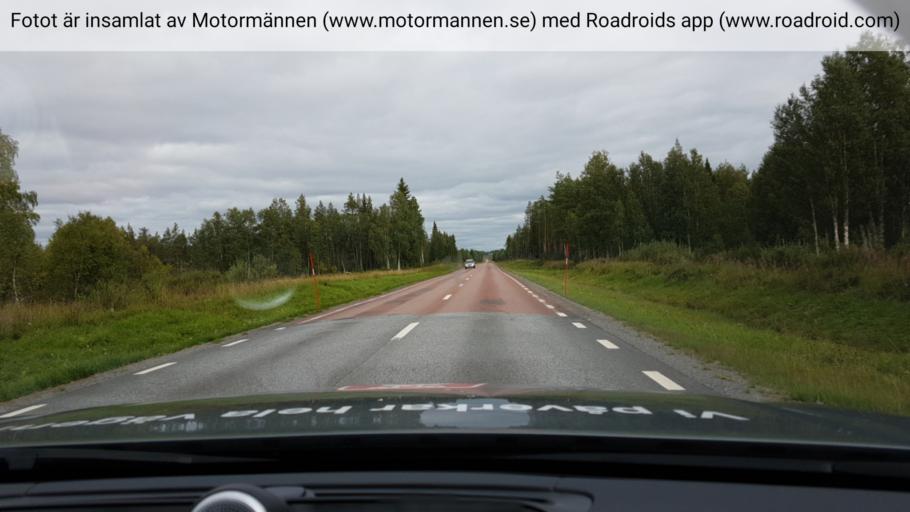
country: SE
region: Jaemtland
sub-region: Stroemsunds Kommun
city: Stroemsund
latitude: 63.7903
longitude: 15.5127
